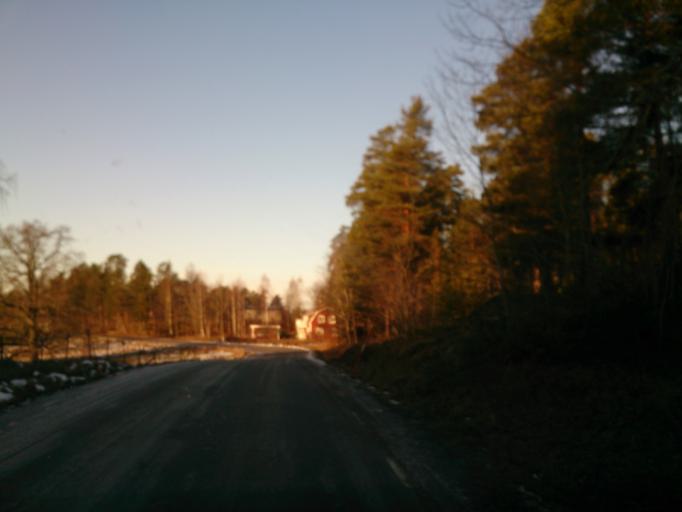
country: SE
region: OEstergoetland
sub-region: Linkopings Kommun
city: Sturefors
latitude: 58.2956
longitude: 15.8756
